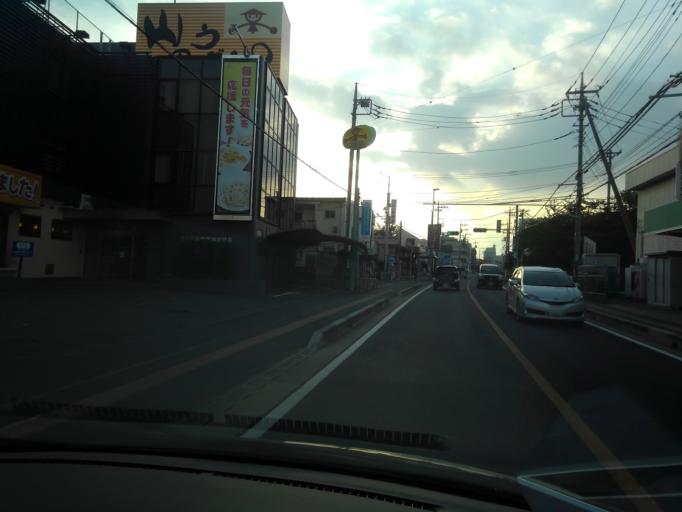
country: JP
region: Saitama
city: Tokorozawa
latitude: 35.7901
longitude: 139.4864
